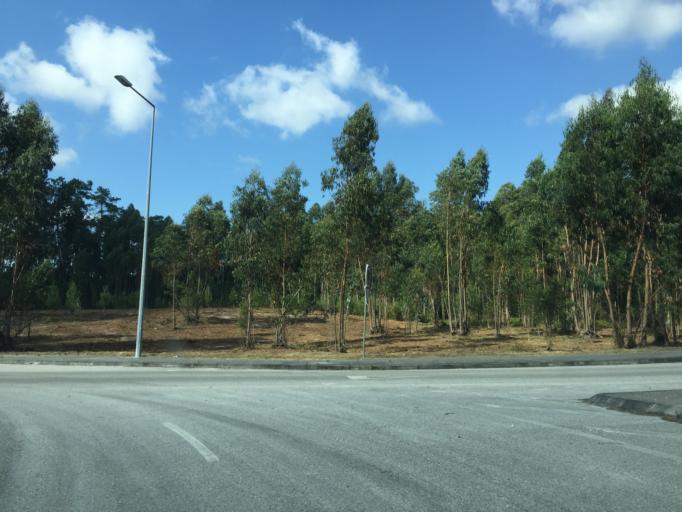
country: PT
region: Leiria
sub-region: Leiria
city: Monte Redondo
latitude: 39.9425
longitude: -8.7981
